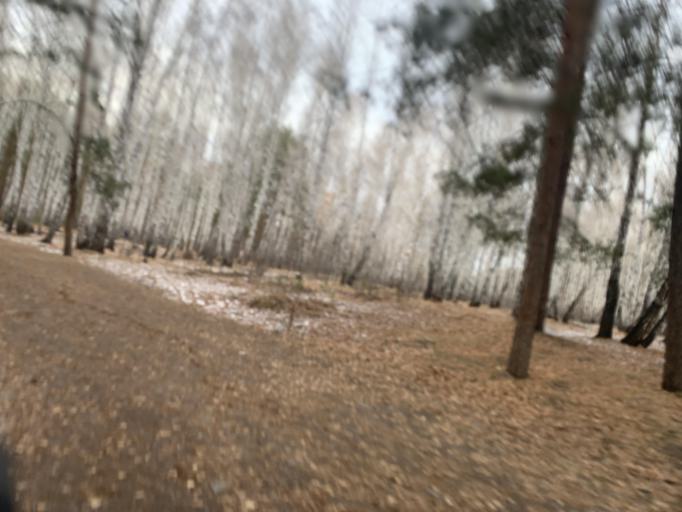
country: RU
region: Chelyabinsk
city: Roshchino
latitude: 55.1966
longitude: 61.2868
